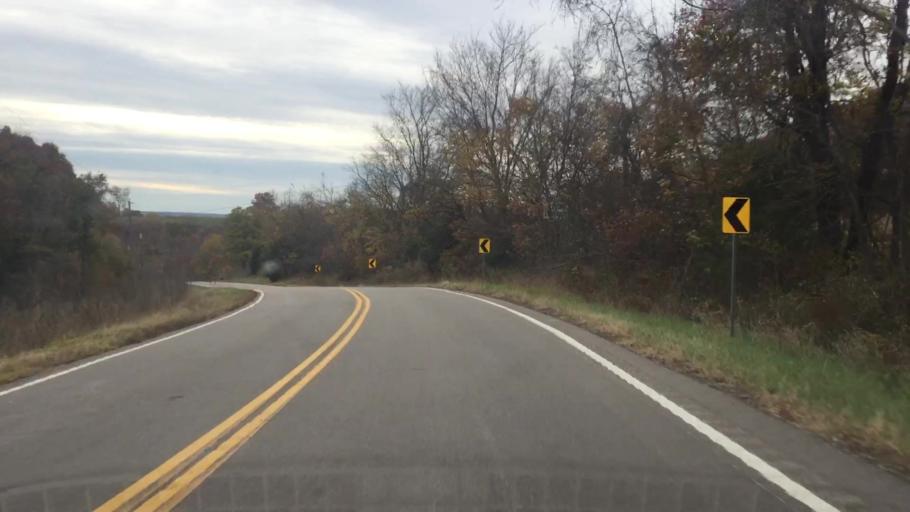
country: US
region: Missouri
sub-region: Callaway County
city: Fulton
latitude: 38.7126
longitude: -91.7373
